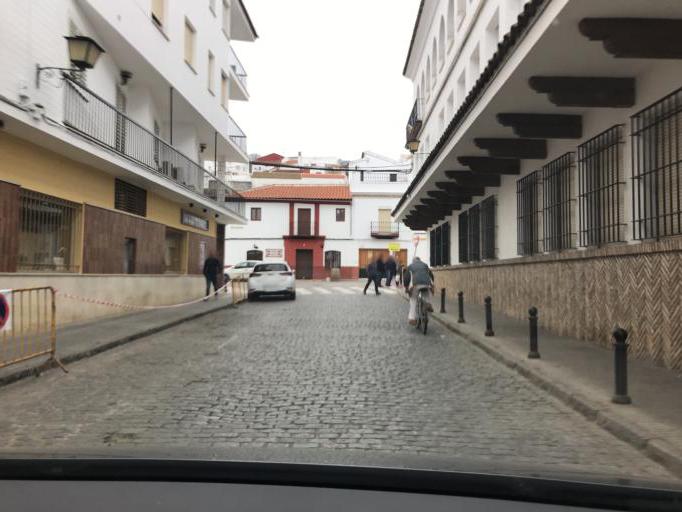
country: ES
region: Andalusia
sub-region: Provincia de Sevilla
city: Constantina
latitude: 37.8751
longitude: -5.6201
